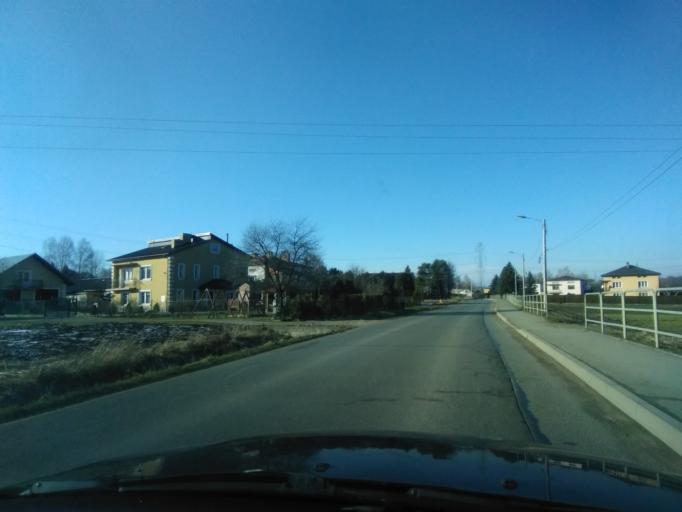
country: PL
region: Subcarpathian Voivodeship
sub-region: Powiat brzozowski
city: Haczow
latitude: 49.6758
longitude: 21.8814
